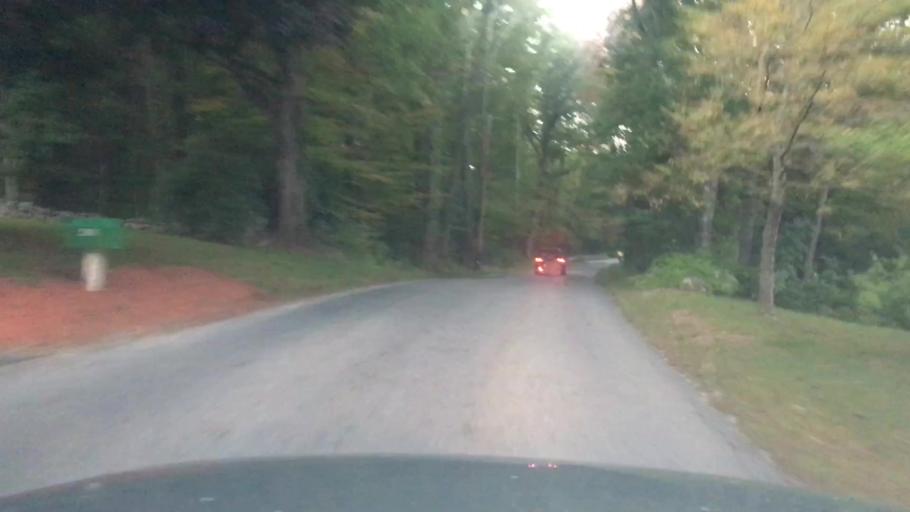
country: US
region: Massachusetts
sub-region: Worcester County
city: Charlton
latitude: 42.1301
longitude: -71.9752
